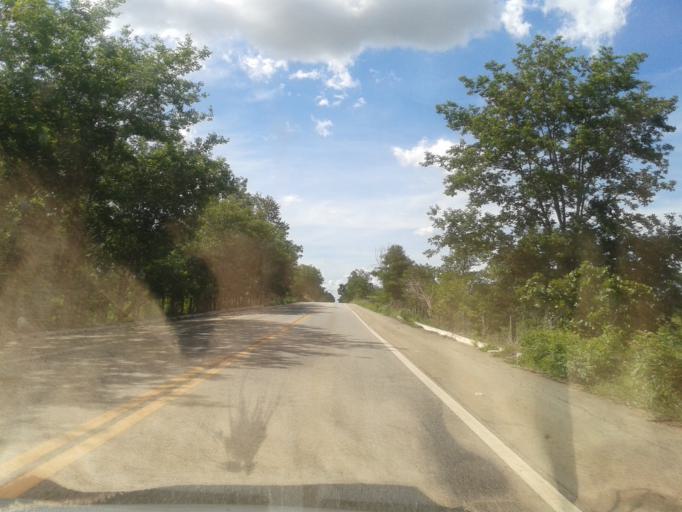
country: BR
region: Goias
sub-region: Itapuranga
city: Itapuranga
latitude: -15.4823
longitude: -50.3308
